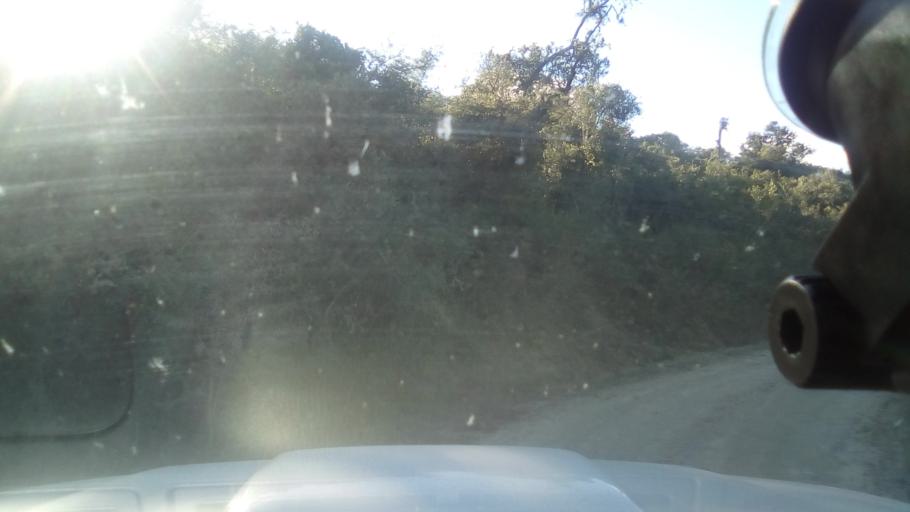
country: ZA
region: Eastern Cape
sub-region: Buffalo City Metropolitan Municipality
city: Bhisho
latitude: -32.7352
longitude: 27.3459
